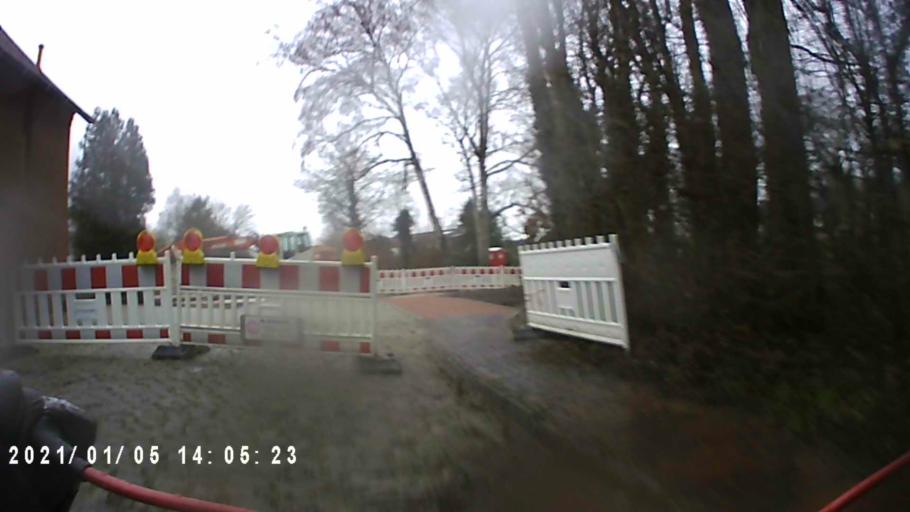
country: DE
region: Lower Saxony
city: Weener
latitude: 53.1637
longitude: 7.3430
